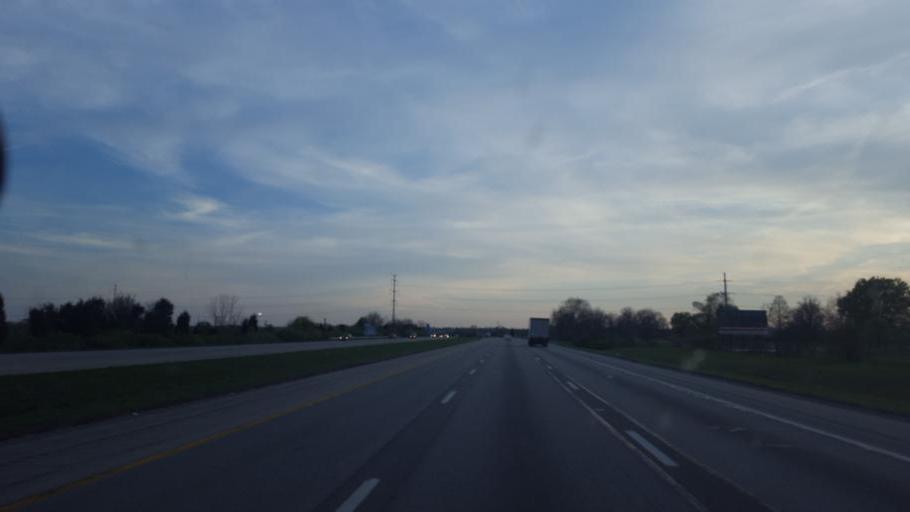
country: US
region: Ohio
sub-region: Warren County
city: Kings Mills
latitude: 39.3466
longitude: -84.2747
